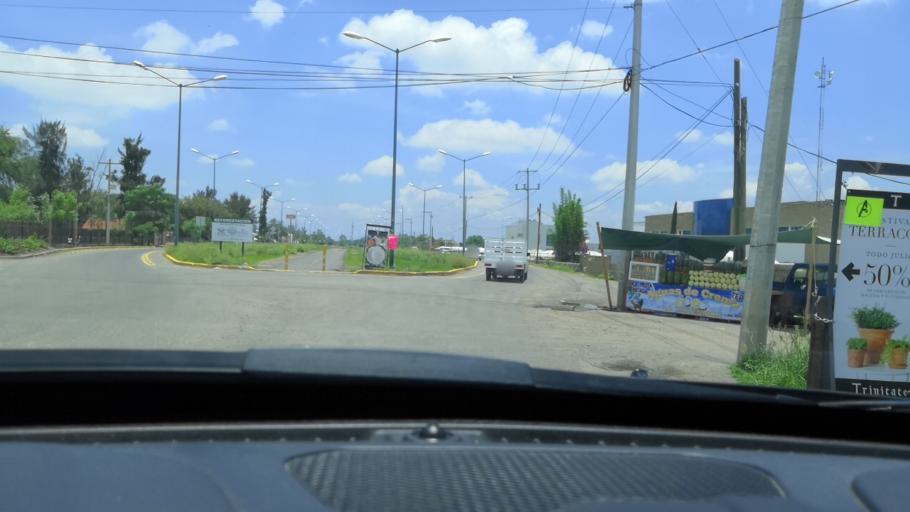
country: MX
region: Guanajuato
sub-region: Silao de la Victoria
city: El Refugio de los Sauces
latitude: 21.0310
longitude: -101.5741
